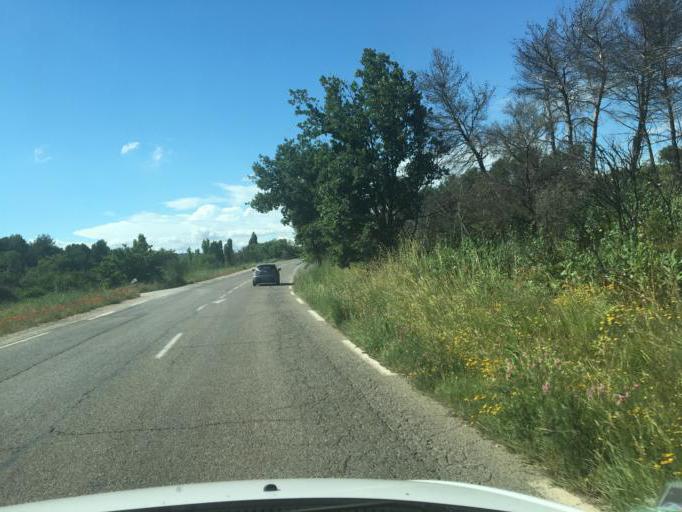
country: FR
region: Provence-Alpes-Cote d'Azur
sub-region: Departement des Bouches-du-Rhone
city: Eguilles
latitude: 43.5335
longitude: 5.3493
